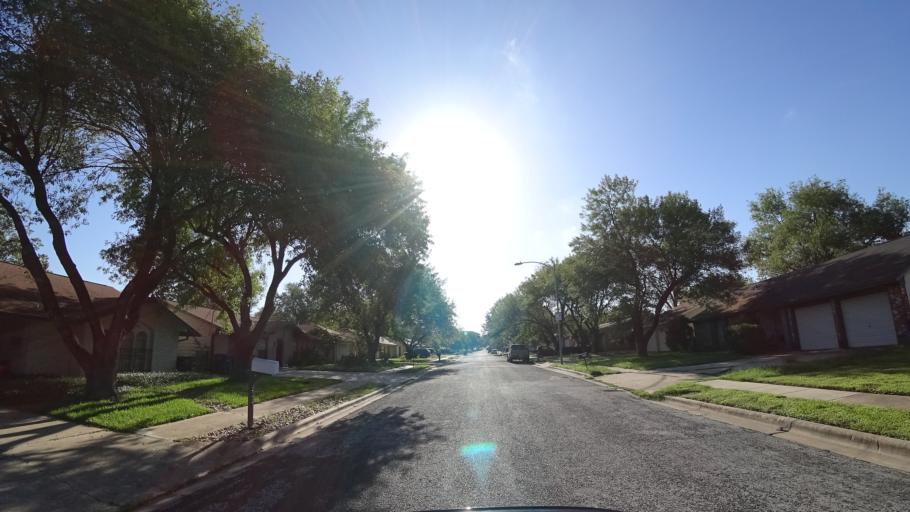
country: US
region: Texas
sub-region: Travis County
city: Shady Hollow
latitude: 30.2117
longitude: -97.8122
